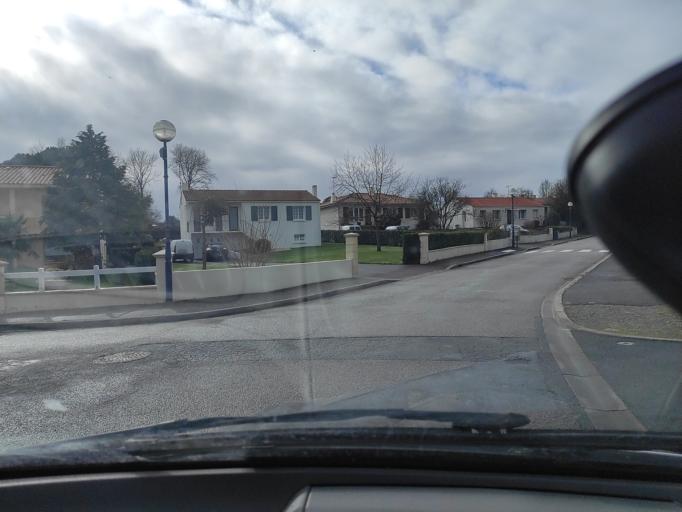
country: FR
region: Pays de la Loire
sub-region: Departement de la Vendee
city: La Boissiere-des-Landes
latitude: 46.5657
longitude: -1.4591
